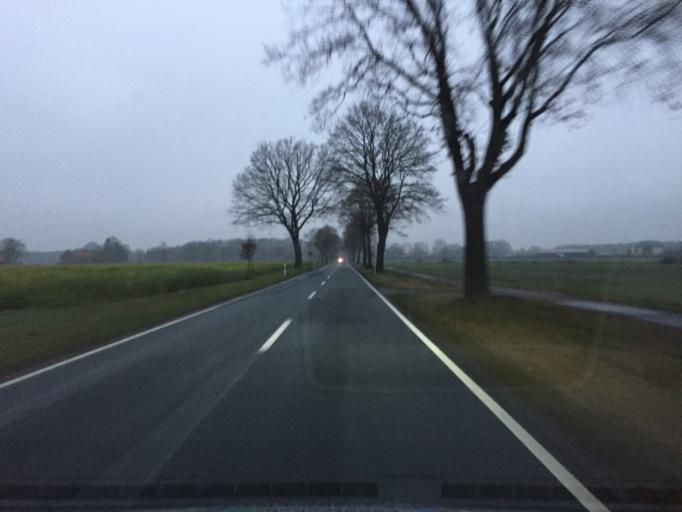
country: DE
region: Lower Saxony
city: Steyerberg
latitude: 52.5884
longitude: 8.9860
